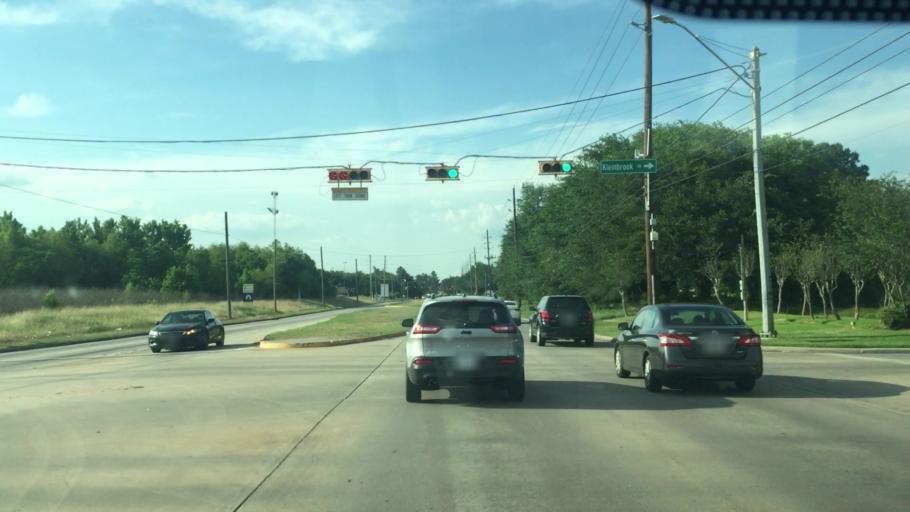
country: US
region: Texas
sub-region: Harris County
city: Hudson
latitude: 29.9568
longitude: -95.4984
